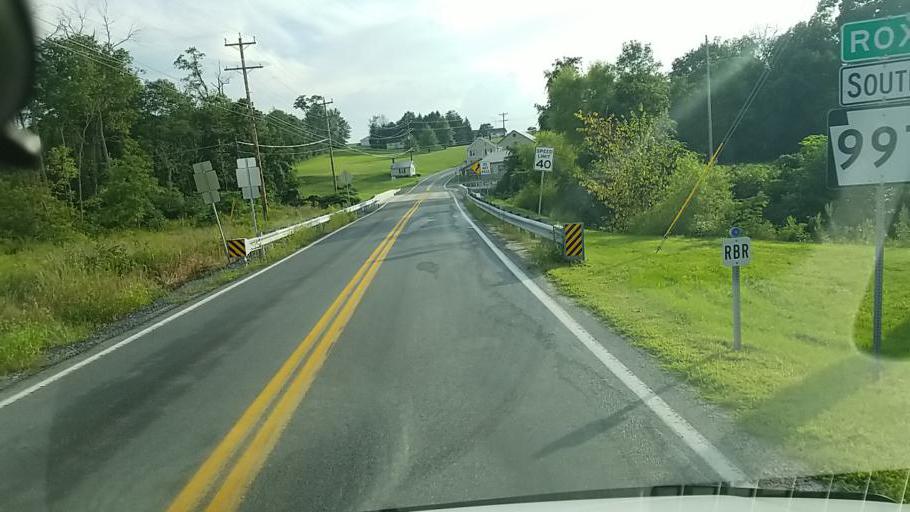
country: US
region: Pennsylvania
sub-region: Cumberland County
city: Newville
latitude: 40.2387
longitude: -77.4445
